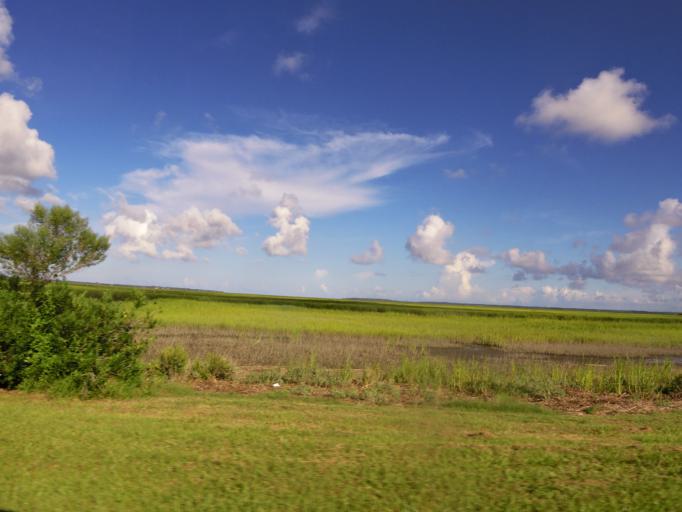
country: US
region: Georgia
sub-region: Glynn County
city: Brunswick
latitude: 31.1423
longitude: -81.4789
